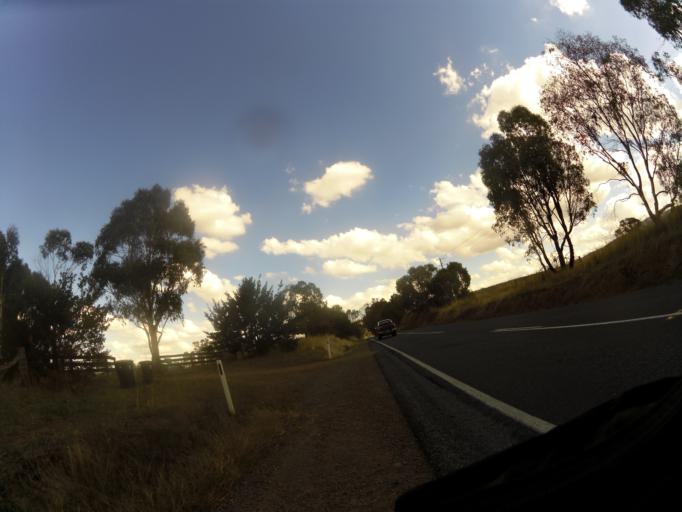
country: AU
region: Victoria
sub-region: Mansfield
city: Mansfield
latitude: -36.9365
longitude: 145.9993
